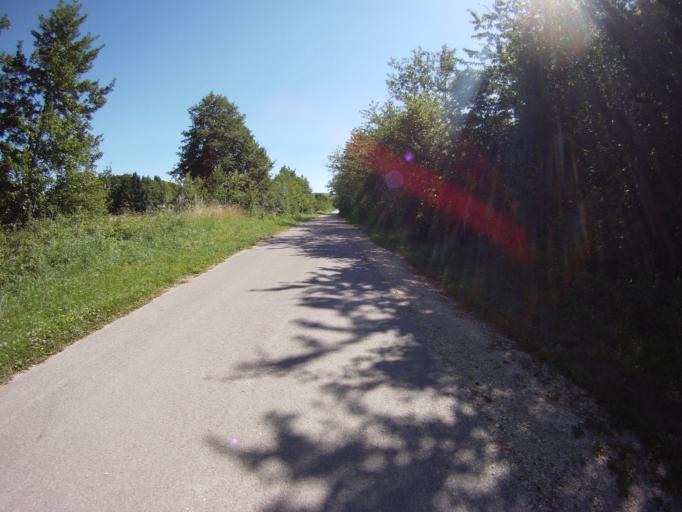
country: FR
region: Champagne-Ardenne
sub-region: Departement de la Marne
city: Dormans
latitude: 49.0858
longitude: 3.6400
